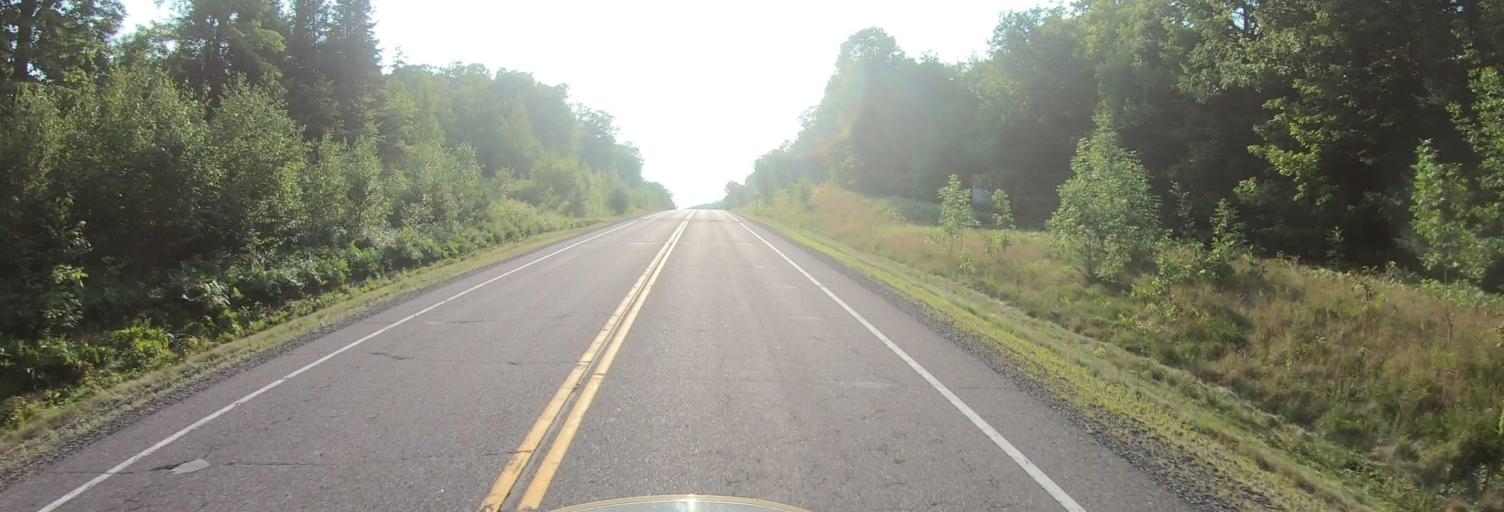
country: US
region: Wisconsin
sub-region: Sawyer County
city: Little Round Lake
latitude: 46.0737
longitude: -91.0542
